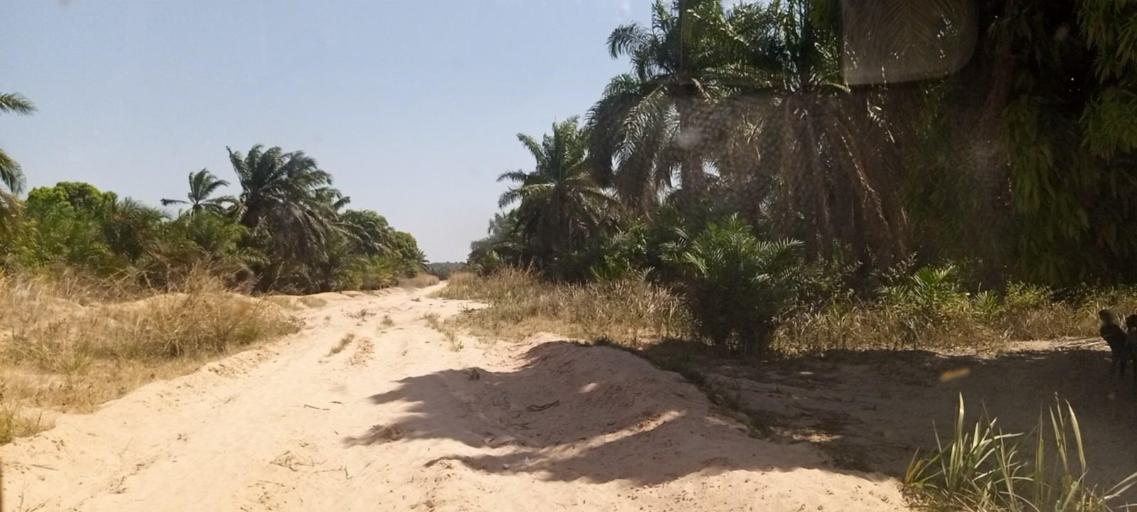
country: CD
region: Kasai-Oriental
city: Kabinda
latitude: -5.9565
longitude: 24.7963
